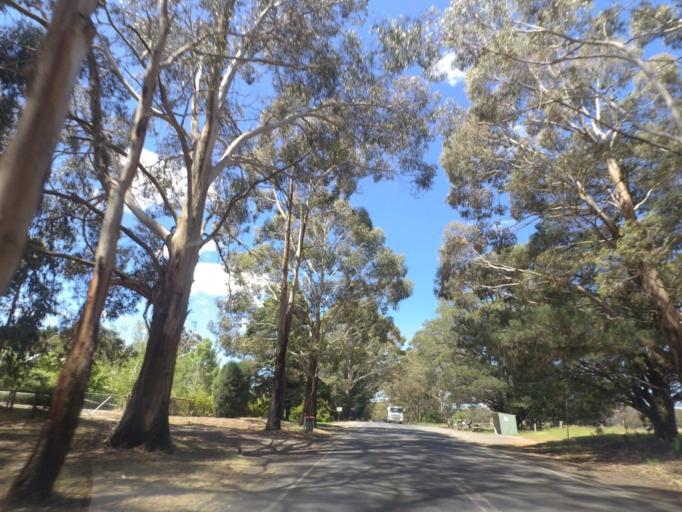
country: AU
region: Victoria
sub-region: Mount Alexander
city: Castlemaine
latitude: -37.3160
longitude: 144.2204
